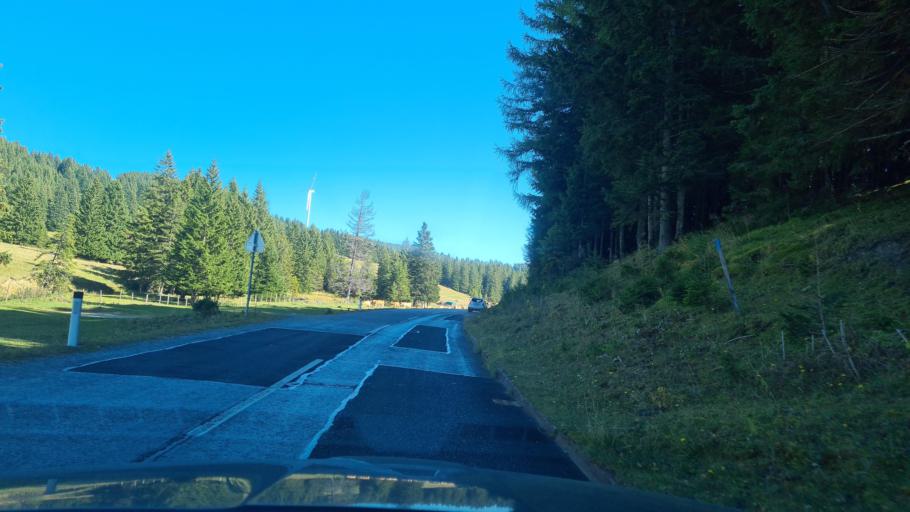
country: AT
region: Styria
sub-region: Politischer Bezirk Weiz
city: Gasen
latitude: 47.3504
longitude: 15.5278
